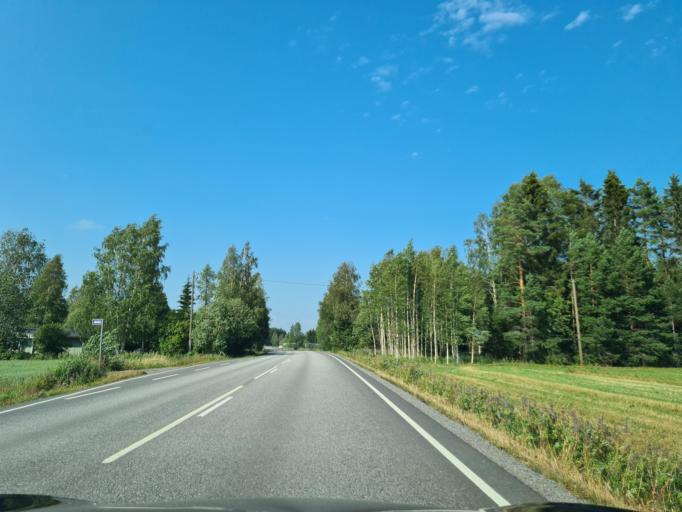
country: FI
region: Satakunta
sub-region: Pohjois-Satakunta
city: Kankaanpaeae
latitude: 61.9382
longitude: 22.5085
